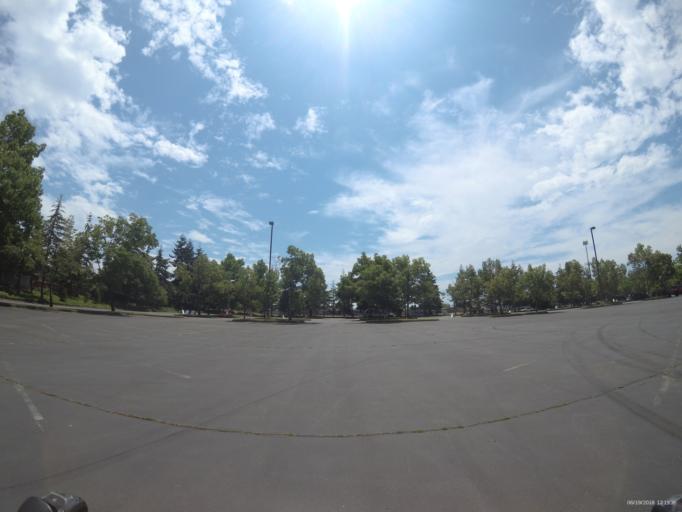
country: US
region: Washington
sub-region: Pierce County
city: Lakewood
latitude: 47.1621
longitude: -122.5108
